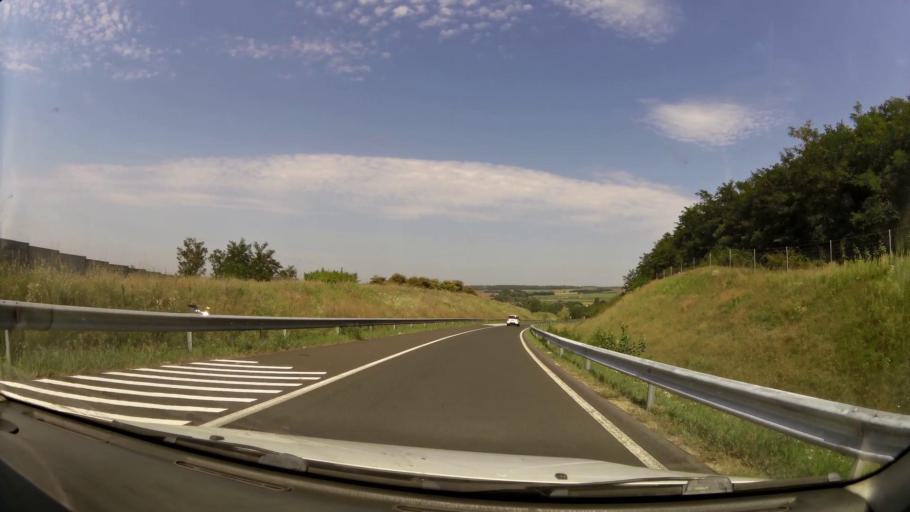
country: HU
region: Pest
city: Pecel
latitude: 47.4877
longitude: 19.3126
